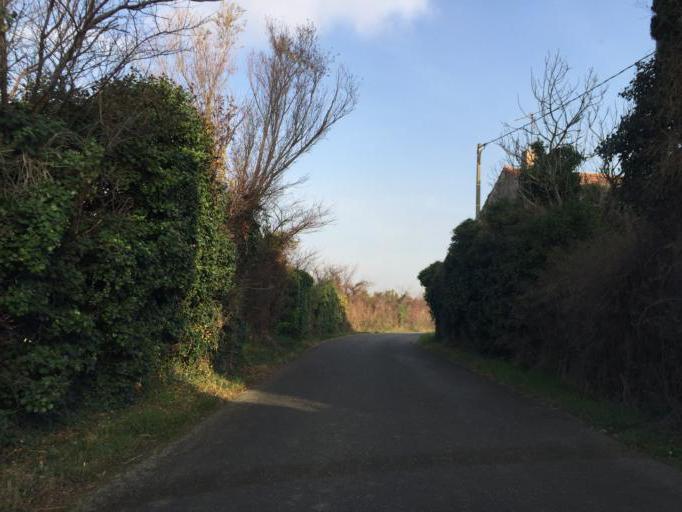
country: FR
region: Provence-Alpes-Cote d'Azur
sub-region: Departement du Vaucluse
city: Courthezon
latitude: 44.0837
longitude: 4.9077
